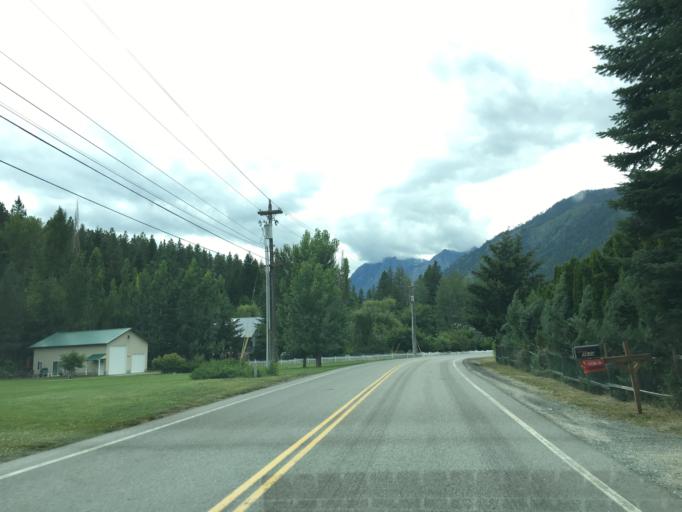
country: US
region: Washington
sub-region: Chelan County
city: Leavenworth
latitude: 47.5918
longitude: -120.6552
